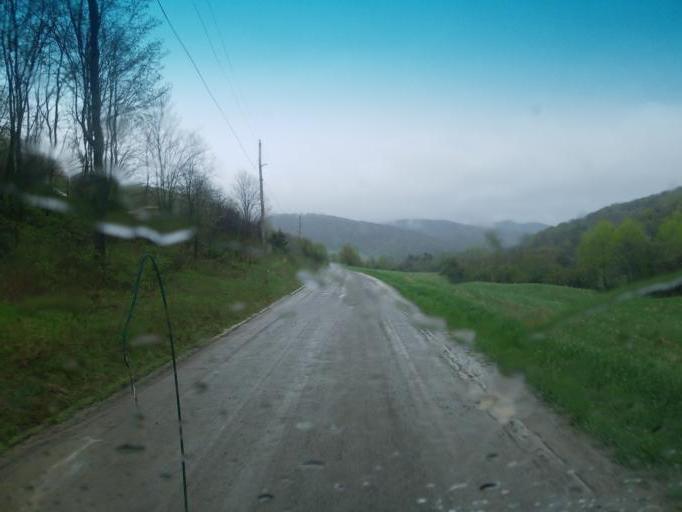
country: US
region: Pennsylvania
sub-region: Tioga County
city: Westfield
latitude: 41.9123
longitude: -77.6335
